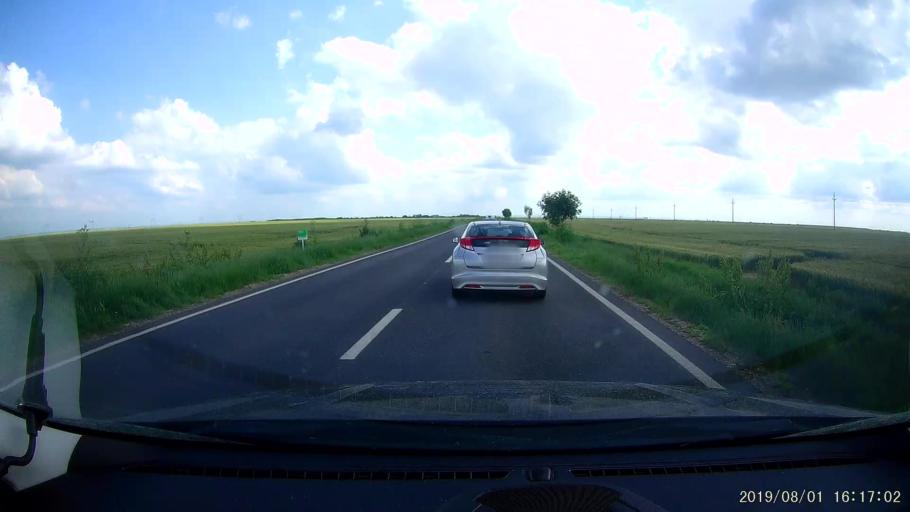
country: RO
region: Calarasi
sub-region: Comuna Stefan Voda
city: Stefan Voda
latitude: 44.3105
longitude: 27.3563
